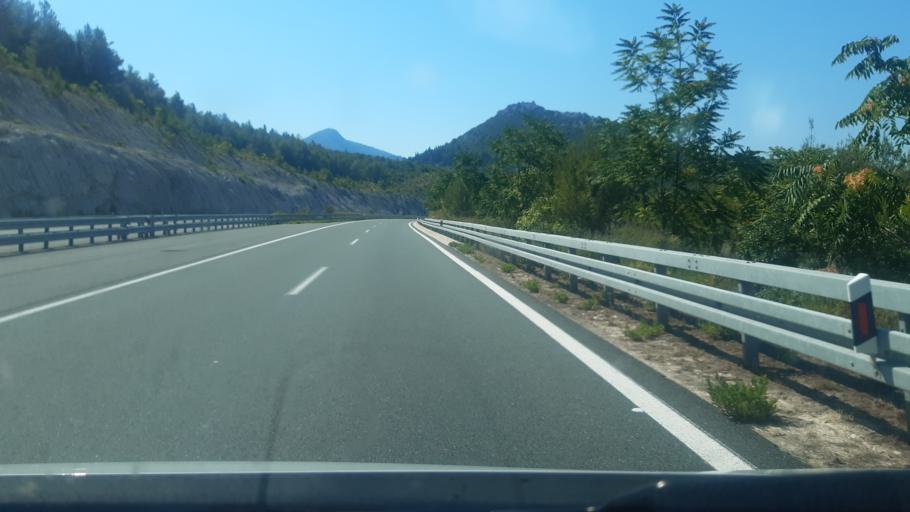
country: BA
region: Federation of Bosnia and Herzegovina
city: Ljubuski
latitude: 43.1342
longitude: 17.4835
